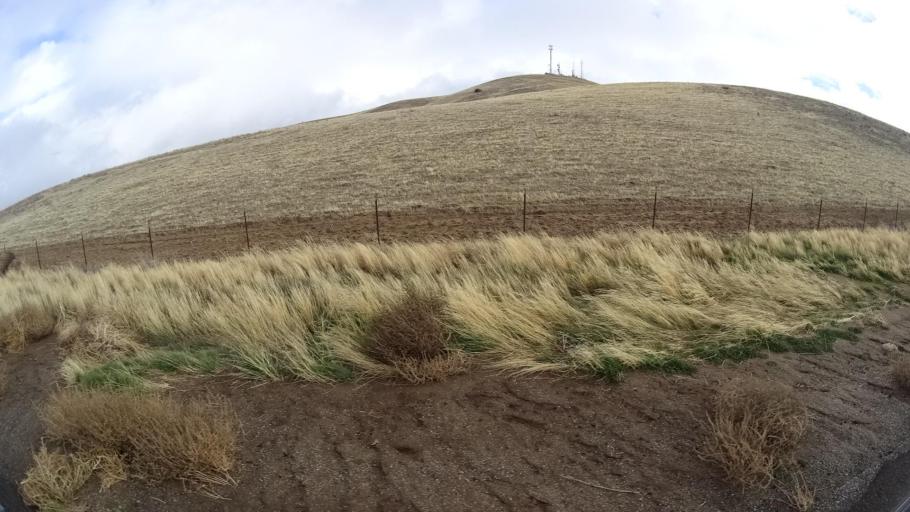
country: US
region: California
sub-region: Kern County
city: Maricopa
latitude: 34.9191
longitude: -119.4127
